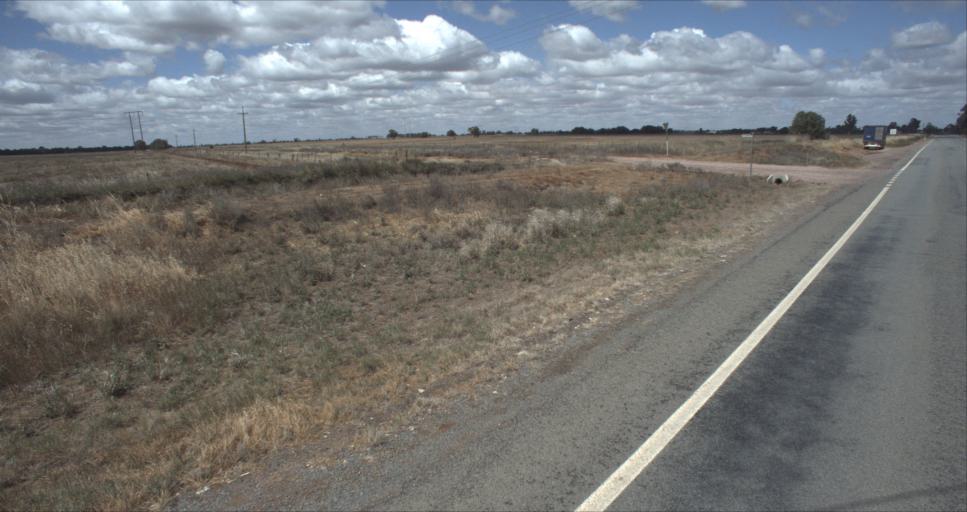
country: AU
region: New South Wales
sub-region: Murrumbidgee Shire
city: Darlington Point
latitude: -34.5102
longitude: 146.1865
